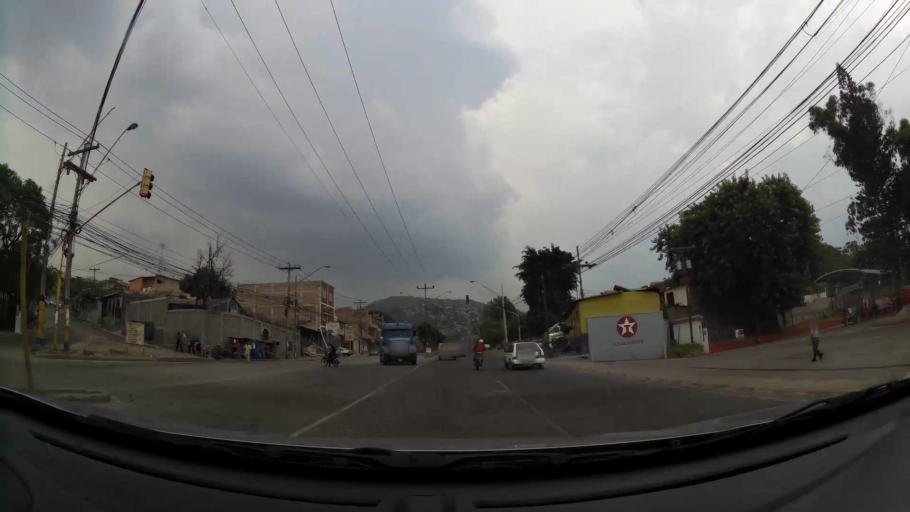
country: HN
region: Francisco Morazan
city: Tegucigalpa
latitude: 14.1015
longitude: -87.2321
